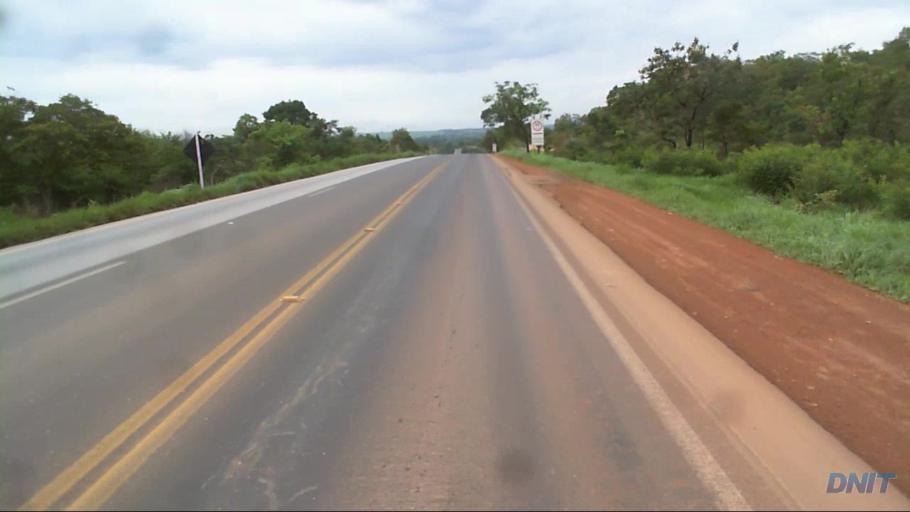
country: BR
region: Goias
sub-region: Uruacu
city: Uruacu
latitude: -14.5728
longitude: -49.1571
